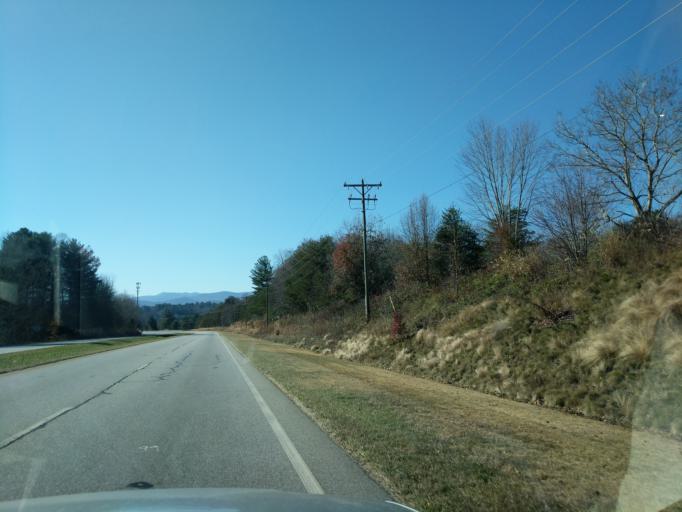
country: US
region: North Carolina
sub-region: Henderson County
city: Mills River
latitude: 35.4054
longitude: -82.5638
